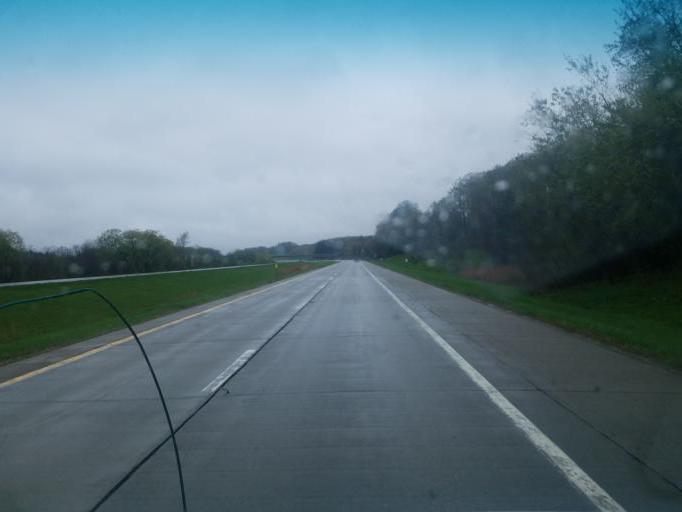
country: US
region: New York
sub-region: Chautauqua County
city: Lakewood
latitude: 42.1527
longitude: -79.4180
